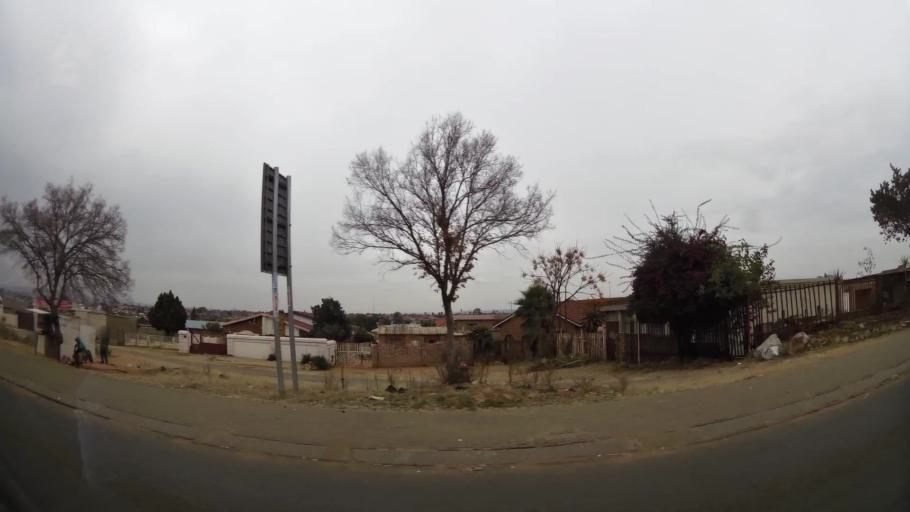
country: ZA
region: Gauteng
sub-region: City of Tshwane Metropolitan Municipality
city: Pretoria
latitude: -25.7045
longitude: 28.3507
